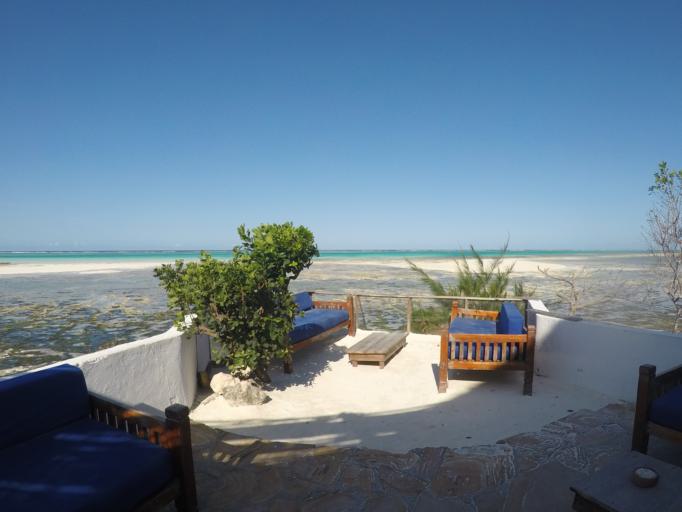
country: TZ
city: Kiwengwa
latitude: -6.1515
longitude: 39.5193
